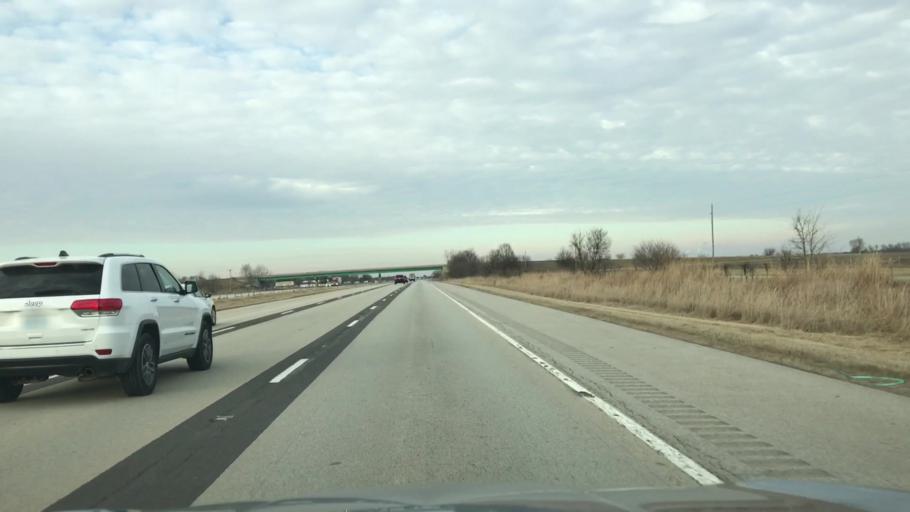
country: US
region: Illinois
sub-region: Sangamon County
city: Chatham
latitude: 39.6443
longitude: -89.6469
